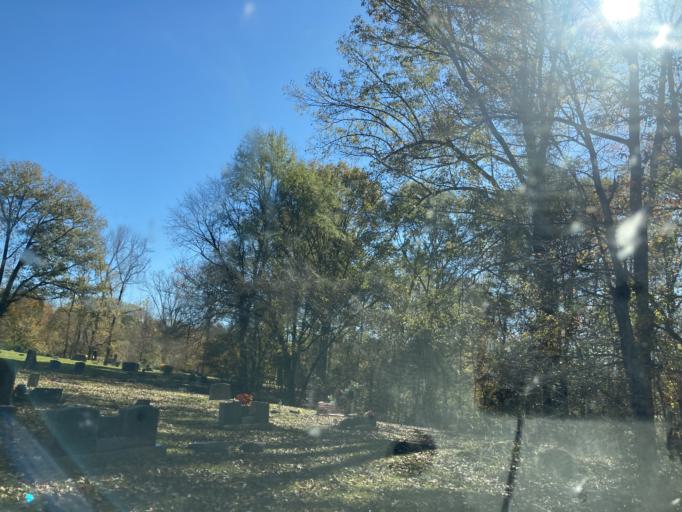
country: US
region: Mississippi
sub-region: Hinds County
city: Lynchburg
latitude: 32.5682
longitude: -90.5112
